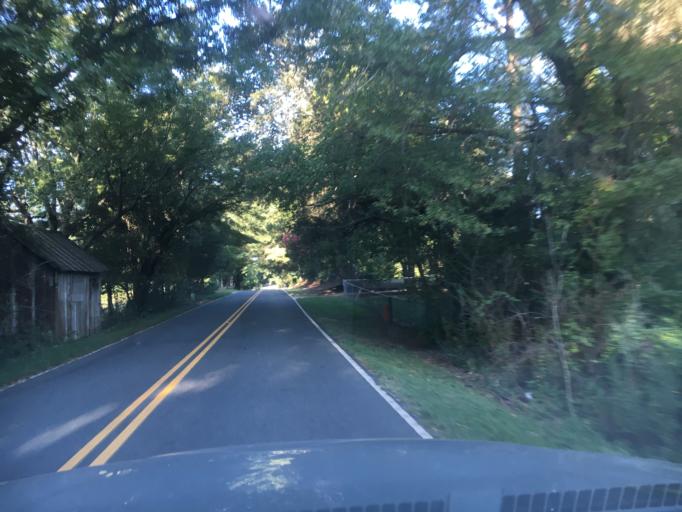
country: US
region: South Carolina
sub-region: Spartanburg County
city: Woodruff
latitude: 34.6360
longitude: -81.9979
